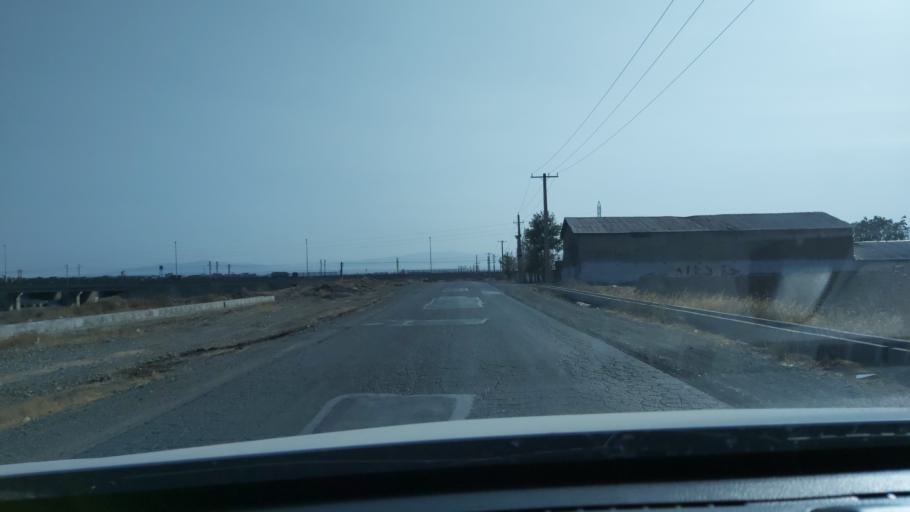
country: IR
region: Alborz
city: Hashtgerd
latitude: 35.9287
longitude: 50.7744
